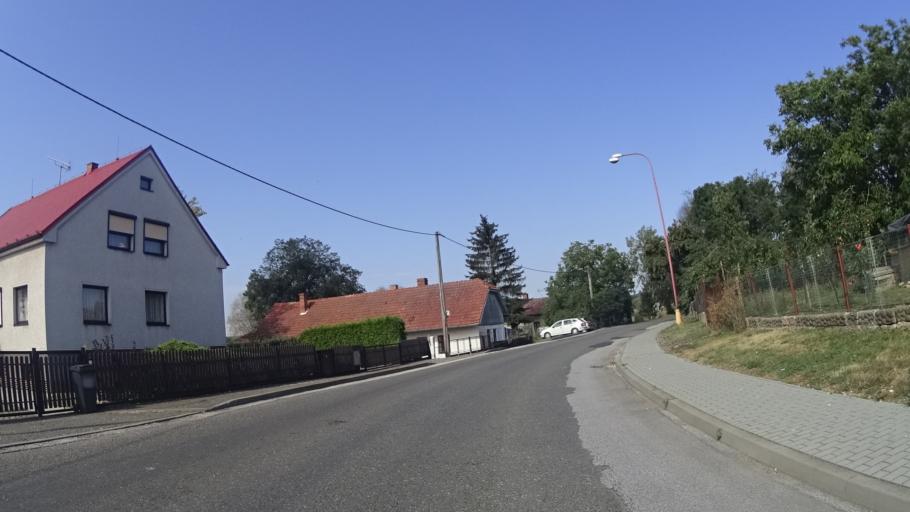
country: CZ
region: Kralovehradecky
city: Novy Bydzov
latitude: 50.2772
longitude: 15.5536
